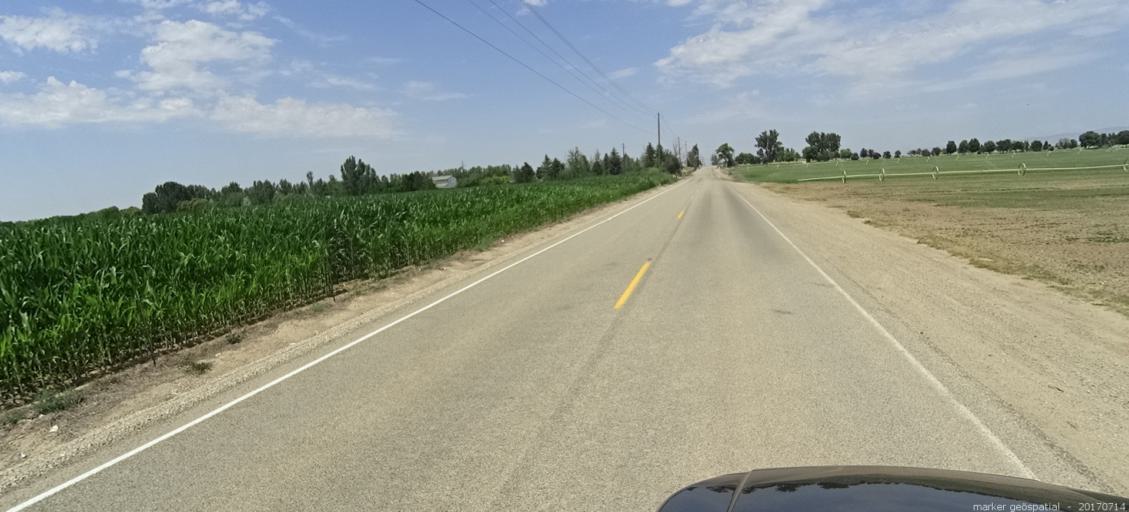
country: US
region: Idaho
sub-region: Ada County
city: Kuna
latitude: 43.5358
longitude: -116.3543
